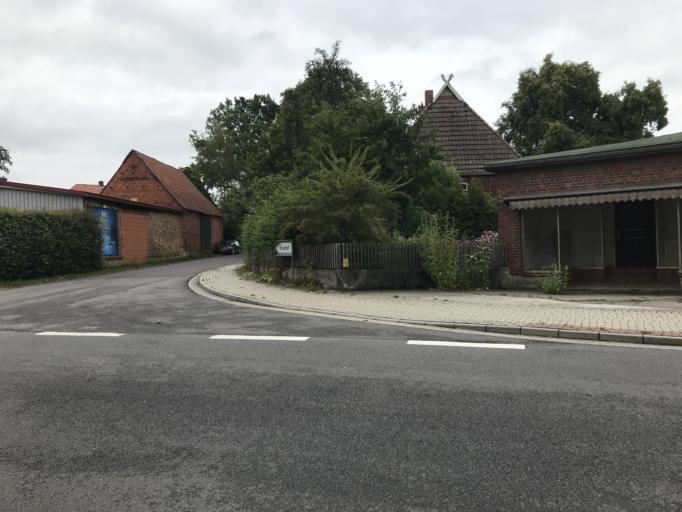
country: DE
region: Lower Saxony
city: Suderburg
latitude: 52.8967
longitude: 10.4528
